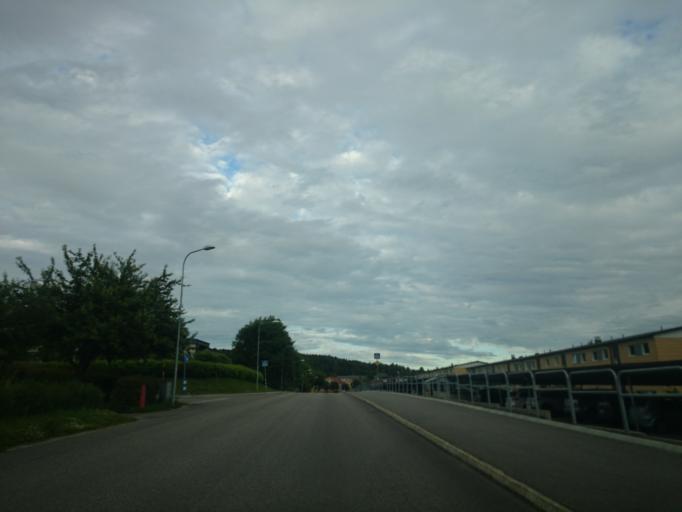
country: SE
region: Vaesternorrland
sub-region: Sundsvalls Kommun
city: Sundsvall
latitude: 62.4064
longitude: 17.2542
